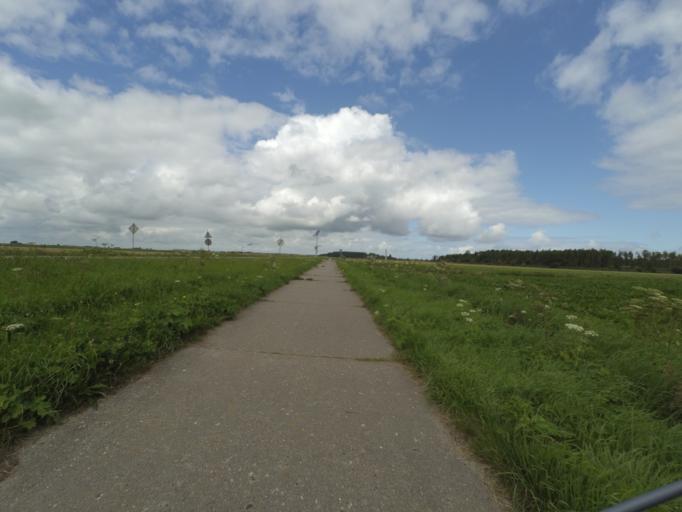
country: NL
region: Groningen
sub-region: Gemeente Zuidhorn
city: Grijpskerk
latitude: 53.3175
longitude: 6.2557
